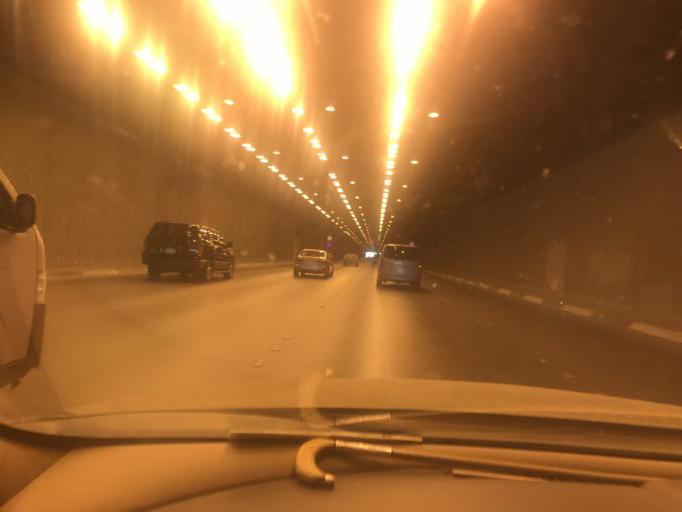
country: SA
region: Ar Riyad
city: Riyadh
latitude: 24.7276
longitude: 46.7126
